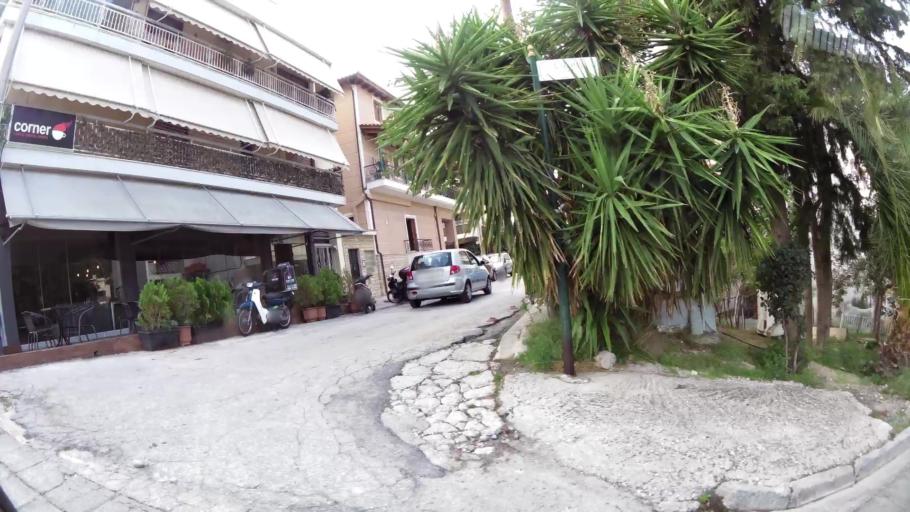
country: GR
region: Attica
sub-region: Nomarchia Athinas
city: Ymittos
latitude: 37.9476
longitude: 23.7635
